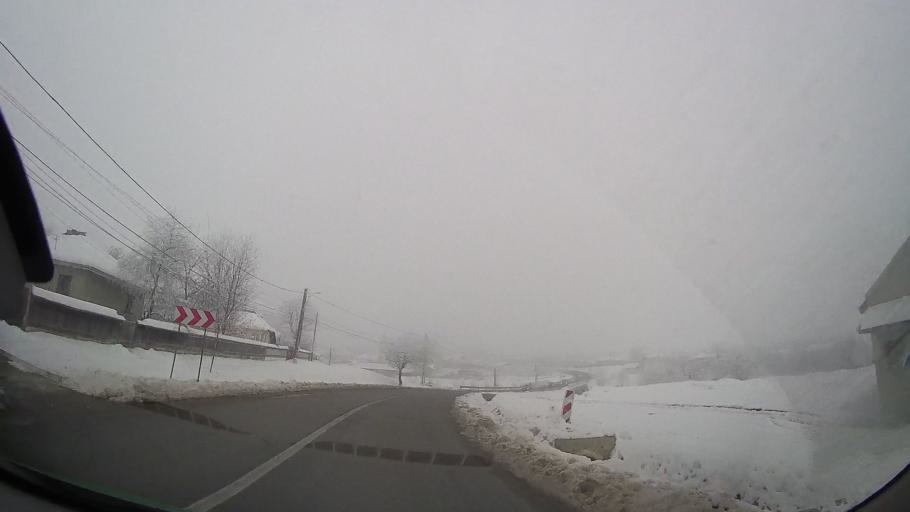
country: RO
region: Iasi
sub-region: Comuna Stolniceni-Prajescu
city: Stolniceni-Prajescu
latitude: 47.1673
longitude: 26.7677
